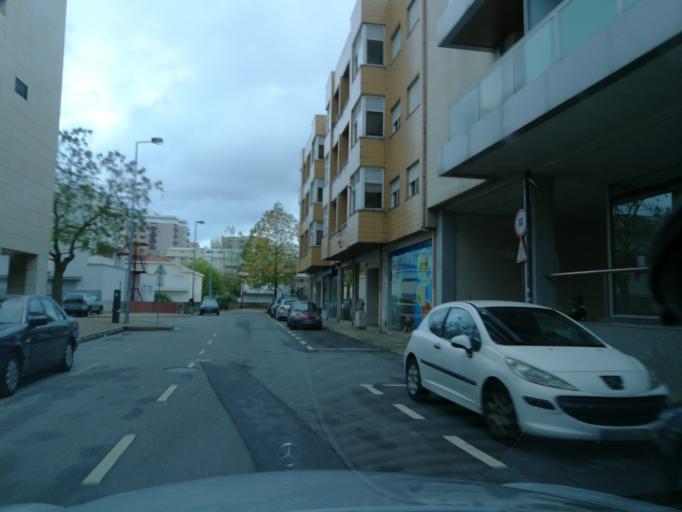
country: PT
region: Braga
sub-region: Braga
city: Braga
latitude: 41.5458
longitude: -8.4148
